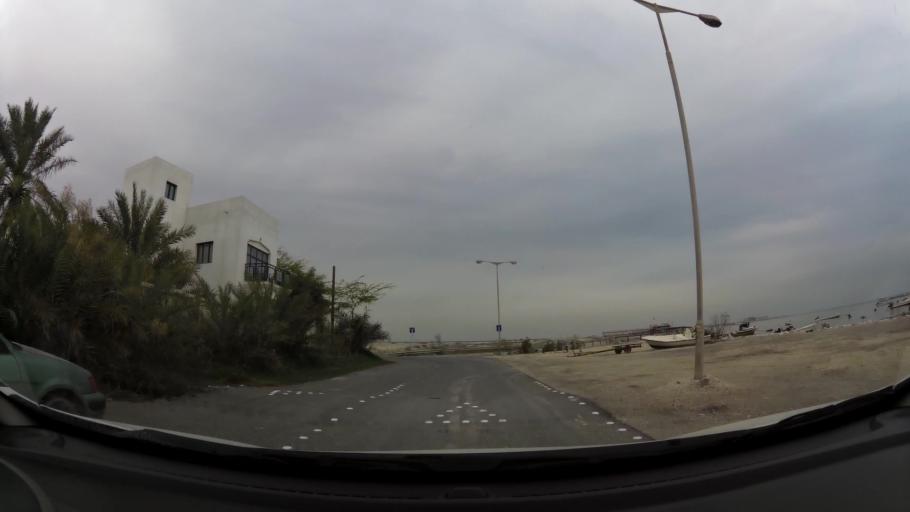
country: BH
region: Northern
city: Ar Rifa'
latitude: 26.0603
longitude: 50.6183
